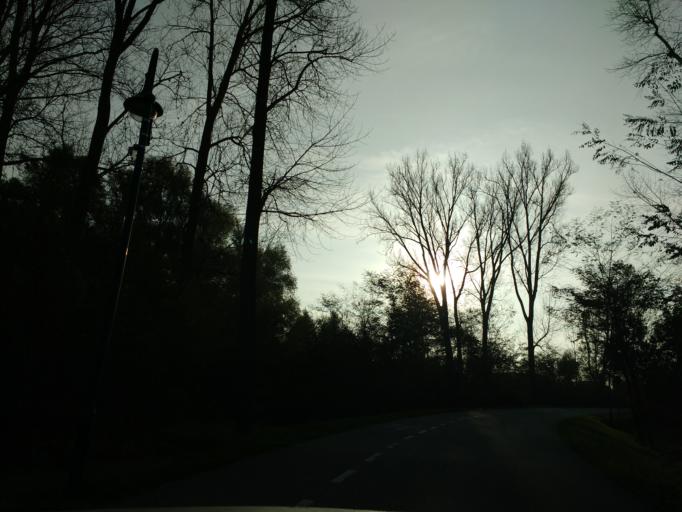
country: DE
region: Mecklenburg-Vorpommern
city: Ostseebad Boltenhagen
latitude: 53.9758
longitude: 11.2441
